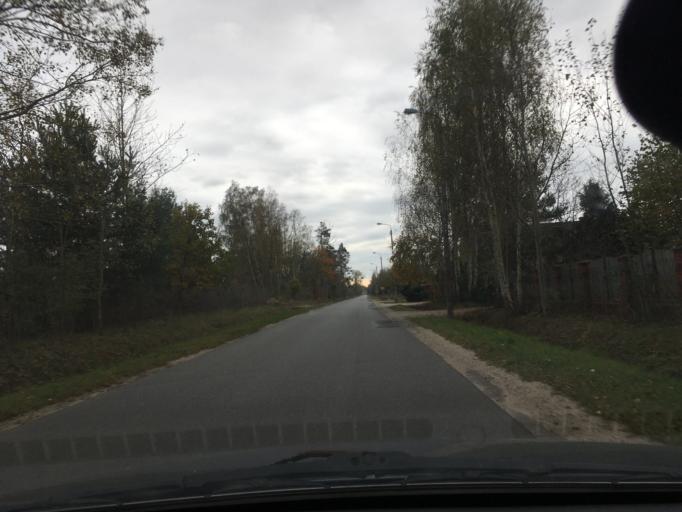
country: PL
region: Lodz Voivodeship
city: Zabia Wola
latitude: 52.0183
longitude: 20.6877
